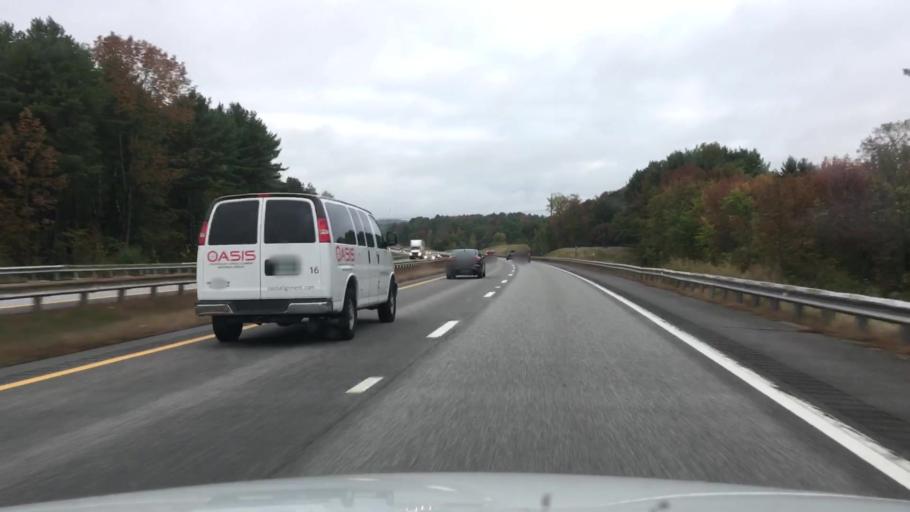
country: US
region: Maine
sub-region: Cumberland County
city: Cumberland Center
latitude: 43.7541
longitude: -70.3043
